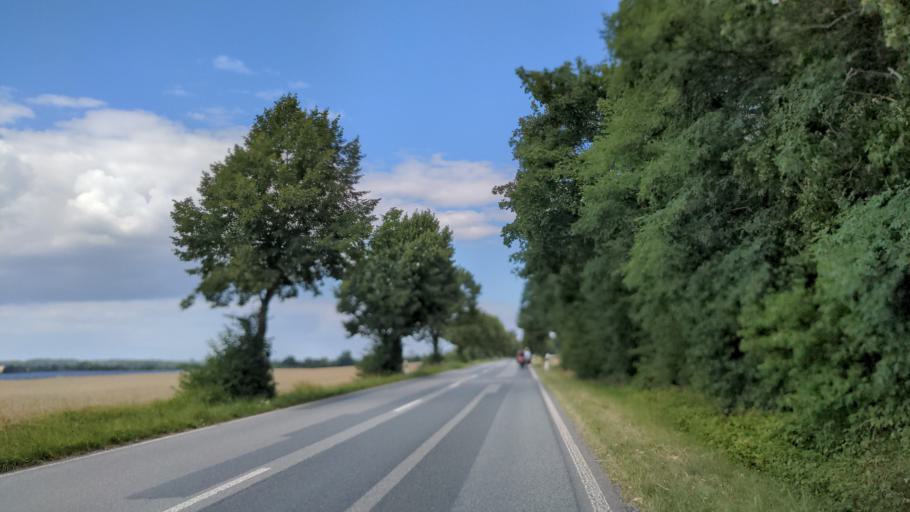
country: DE
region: Schleswig-Holstein
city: Beschendorf
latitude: 54.1698
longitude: 10.8737
